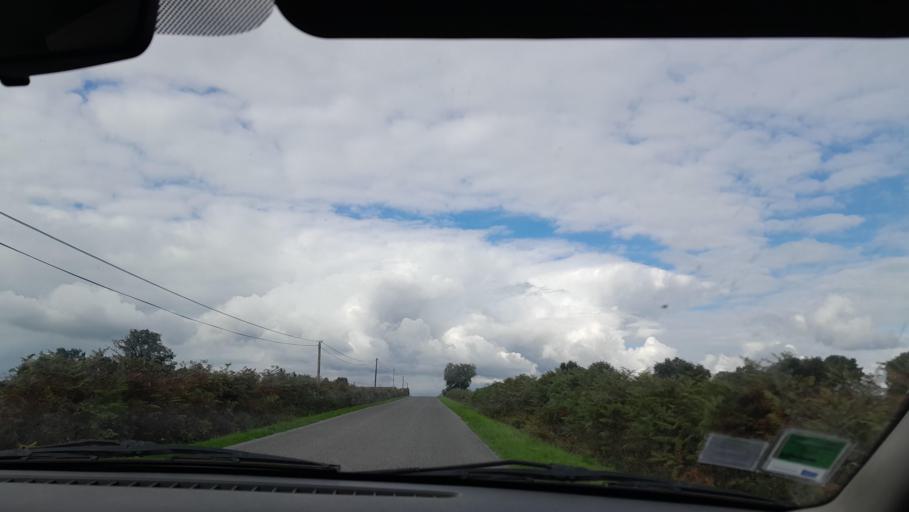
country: FR
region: Brittany
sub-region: Departement d'Ille-et-Vilaine
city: Le Pertre
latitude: 47.9711
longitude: -1.0416
